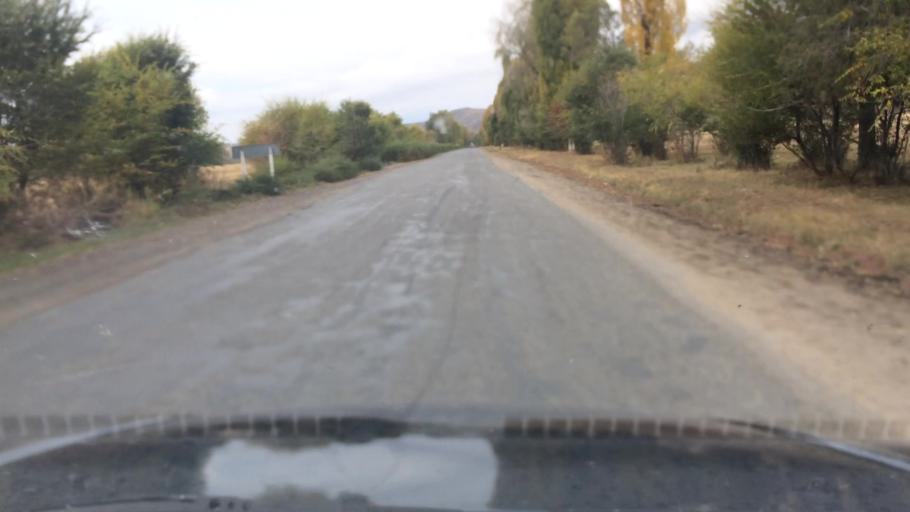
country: KG
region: Ysyk-Koel
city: Pokrovka
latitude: 42.7372
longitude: 77.9301
